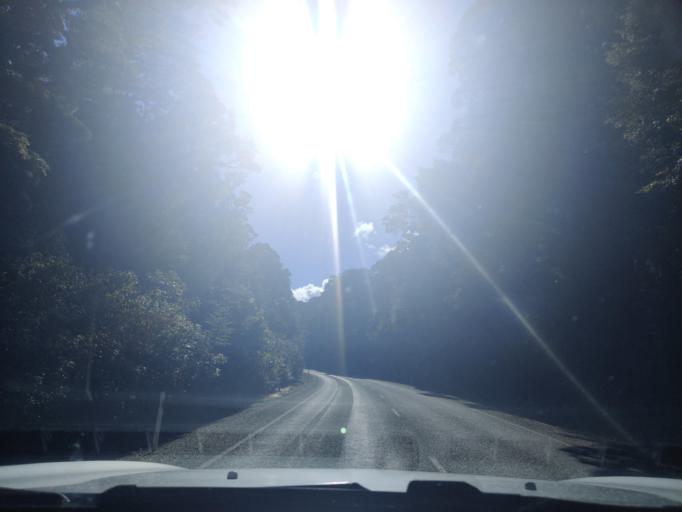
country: NZ
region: Otago
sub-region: Queenstown-Lakes District
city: Wanaka
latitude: -44.1119
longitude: 169.3492
